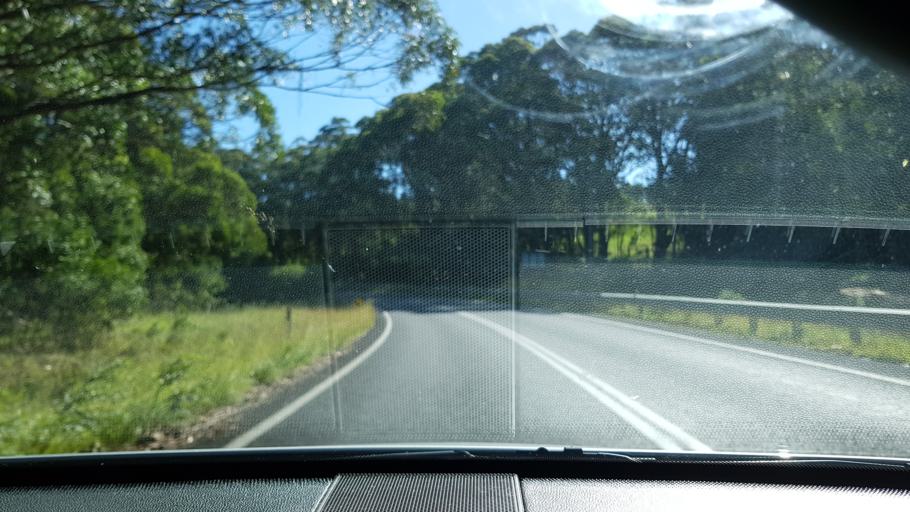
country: AU
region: New South Wales
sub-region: Lithgow
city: Bowenfels
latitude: -33.6392
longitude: 150.0557
